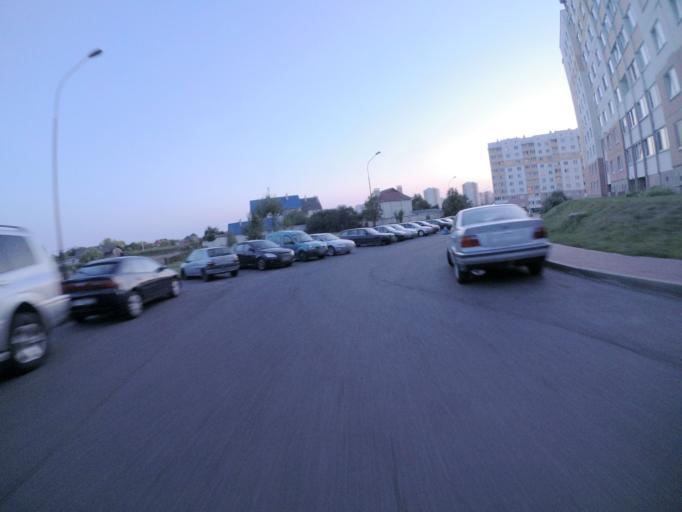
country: BY
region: Grodnenskaya
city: Hrodna
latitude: 53.7112
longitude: 23.8679
